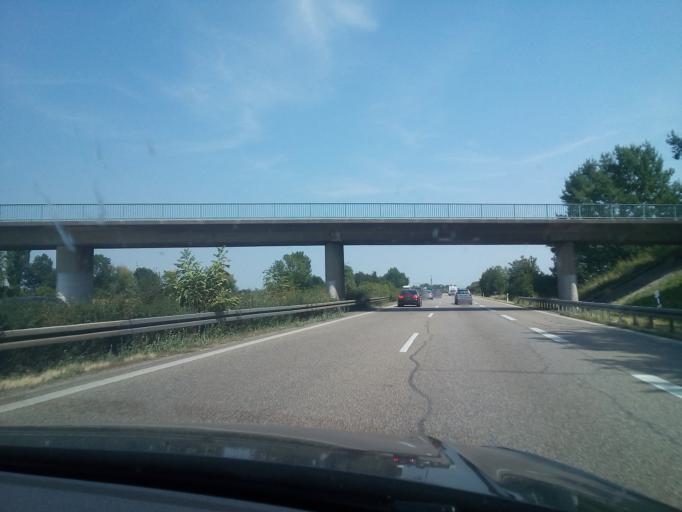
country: DE
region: Baden-Wuerttemberg
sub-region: Freiburg Region
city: Schwanau
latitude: 48.3687
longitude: 7.8049
